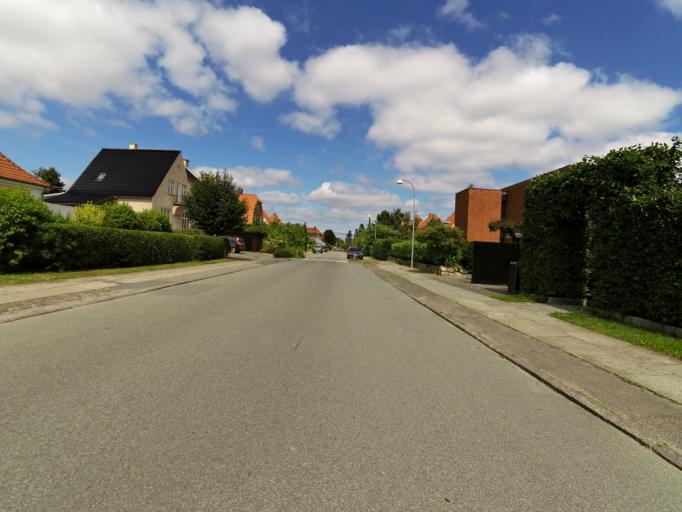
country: DK
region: Capital Region
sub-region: Gladsaxe Municipality
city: Buddinge
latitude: 55.7320
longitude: 12.5102
